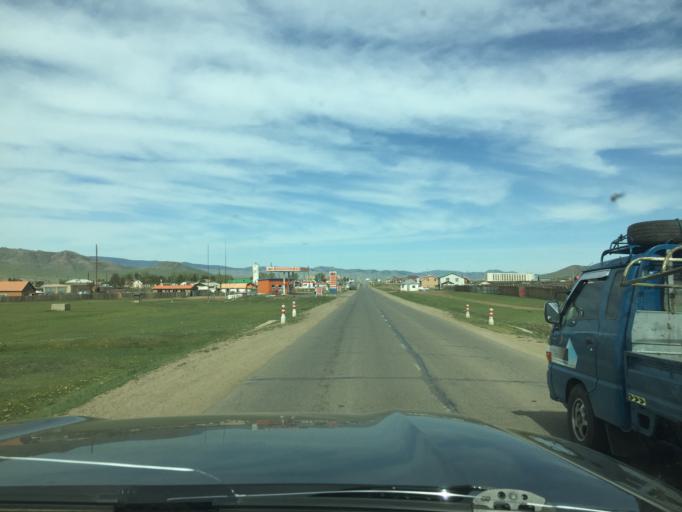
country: MN
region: Central Aimak
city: Ihsueuej
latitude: 48.2199
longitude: 106.3011
